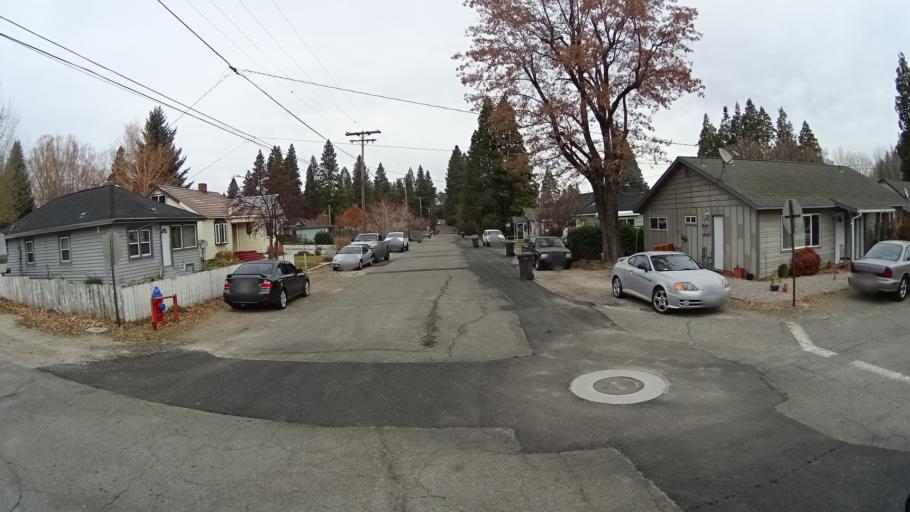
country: US
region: California
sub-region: Siskiyou County
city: Weed
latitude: 41.4153
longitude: -122.3858
